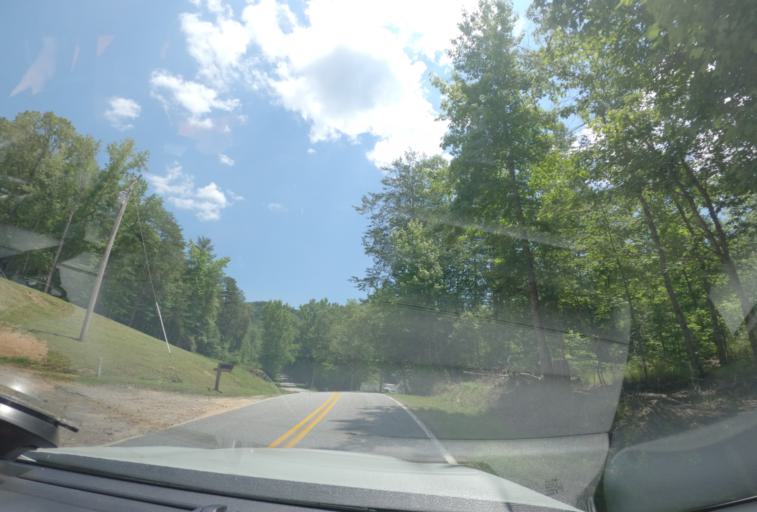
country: US
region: South Carolina
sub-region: Pickens County
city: Pickens
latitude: 34.9966
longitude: -82.8236
